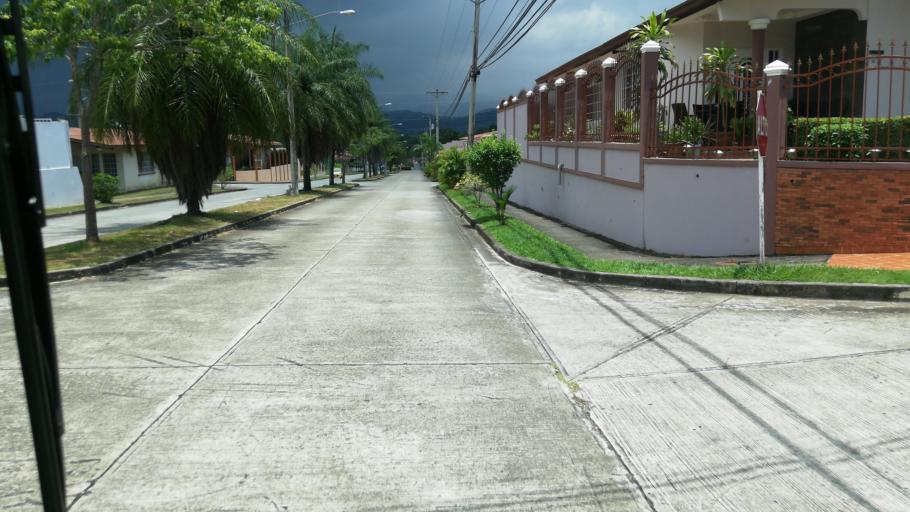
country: PA
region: Panama
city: San Miguelito
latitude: 9.0778
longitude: -79.4504
